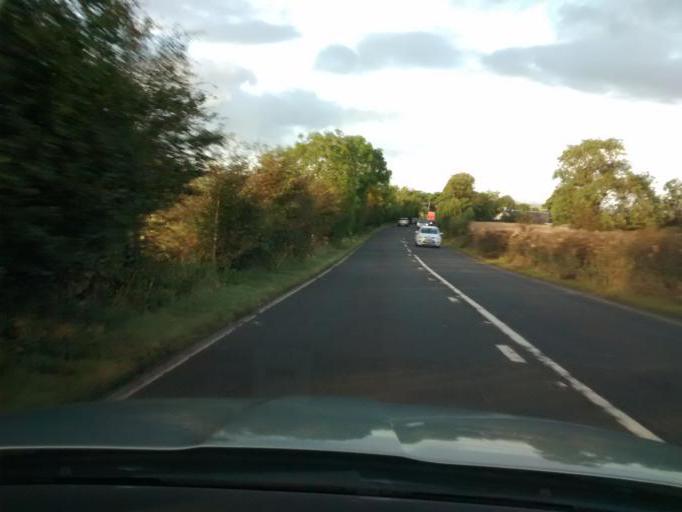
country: GB
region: Scotland
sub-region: Renfrewshire
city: Lochwinnoch
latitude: 55.7940
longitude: -4.5989
